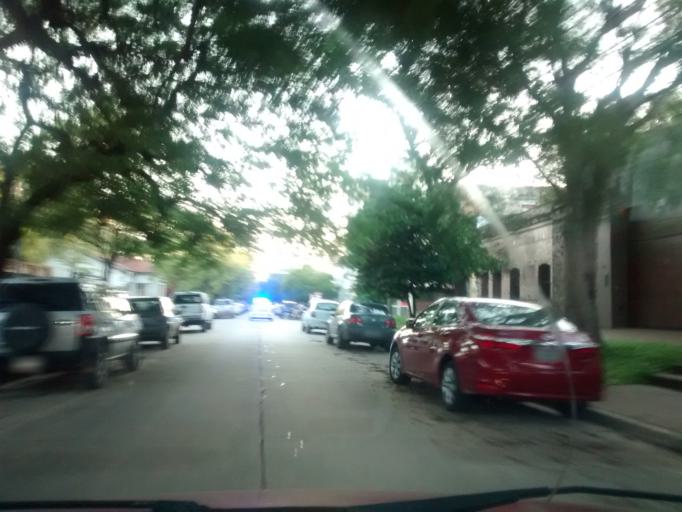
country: AR
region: Chaco
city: Resistencia
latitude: -27.4438
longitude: -58.9835
